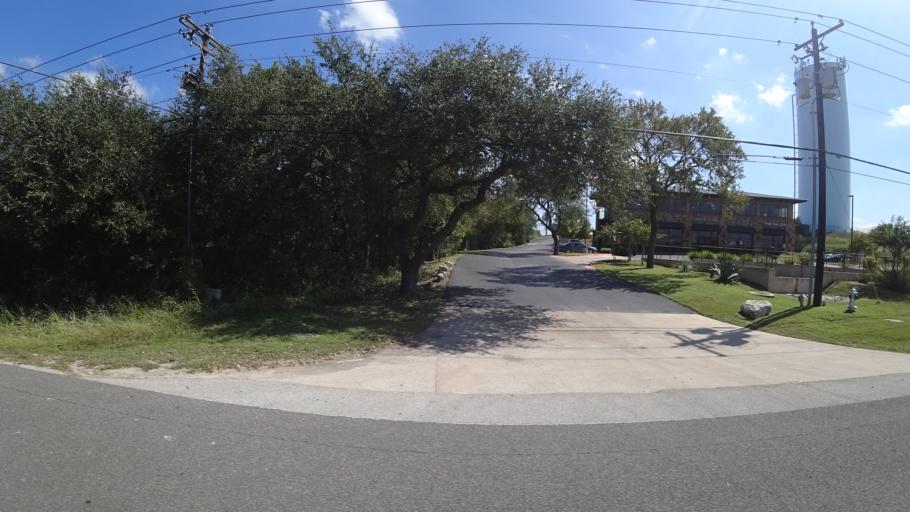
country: US
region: Texas
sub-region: Travis County
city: Lakeway
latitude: 30.3742
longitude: -97.9471
